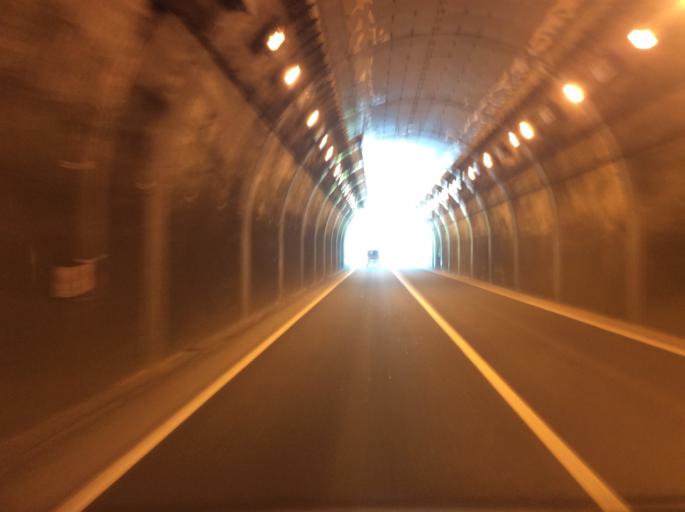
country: JP
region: Fukushima
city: Iwaki
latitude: 37.1638
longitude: 140.9951
